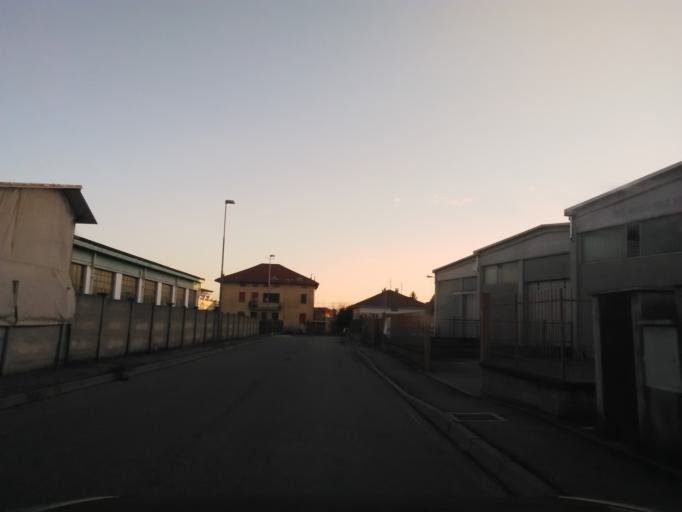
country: IT
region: Piedmont
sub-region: Provincia di Biella
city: Ponderano
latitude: 45.5439
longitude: 8.0543
